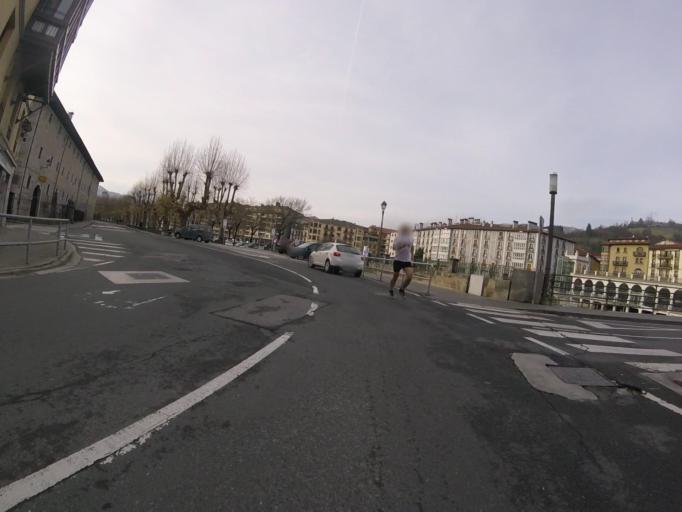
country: ES
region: Basque Country
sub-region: Provincia de Guipuzcoa
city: Tolosa
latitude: 43.1368
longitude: -2.0719
